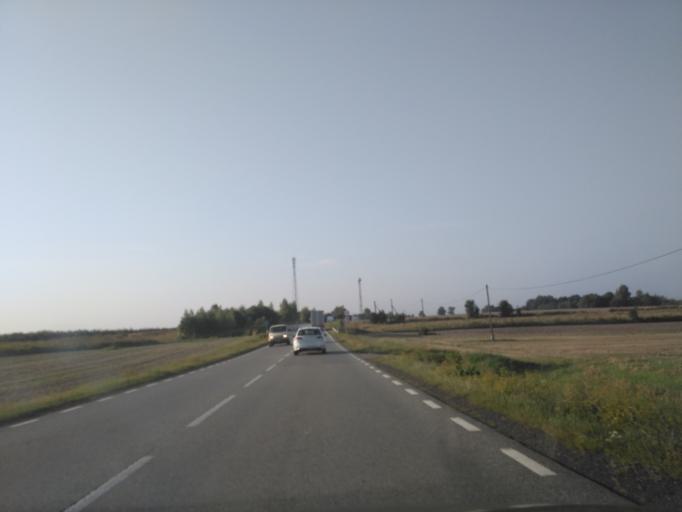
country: PL
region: Lublin Voivodeship
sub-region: Powiat janowski
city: Modliborzyce
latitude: 50.7723
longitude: 22.3251
